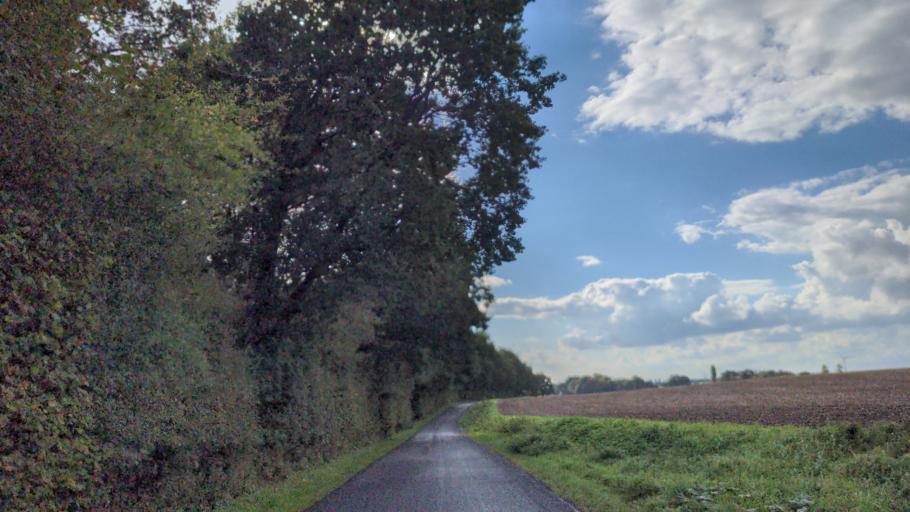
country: DE
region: Schleswig-Holstein
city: Stockelsdorf
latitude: 53.9271
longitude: 10.6252
